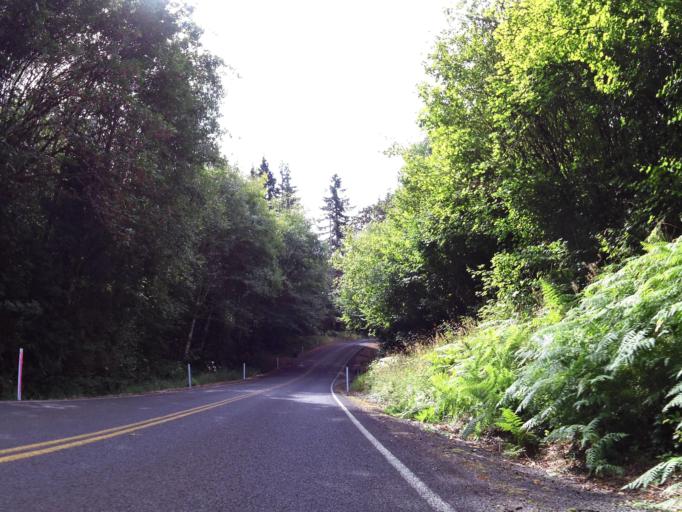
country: US
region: Washington
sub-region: Lewis County
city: Napavine
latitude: 46.5954
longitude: -122.9711
